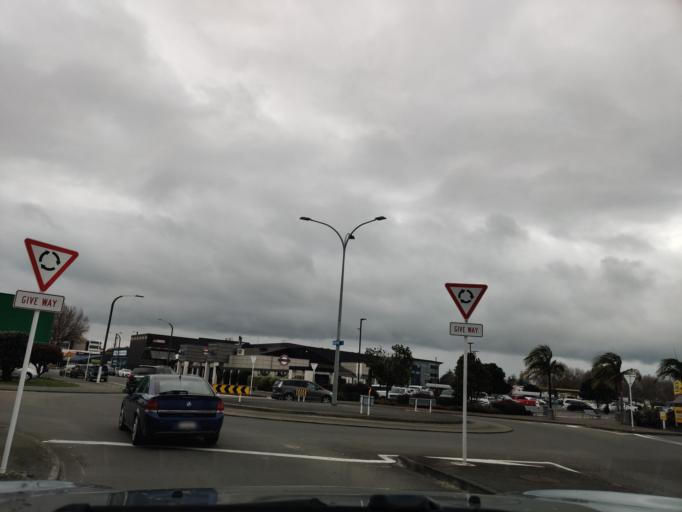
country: NZ
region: Hawke's Bay
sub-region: Napier City
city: Napier
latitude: -39.4935
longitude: 176.9127
